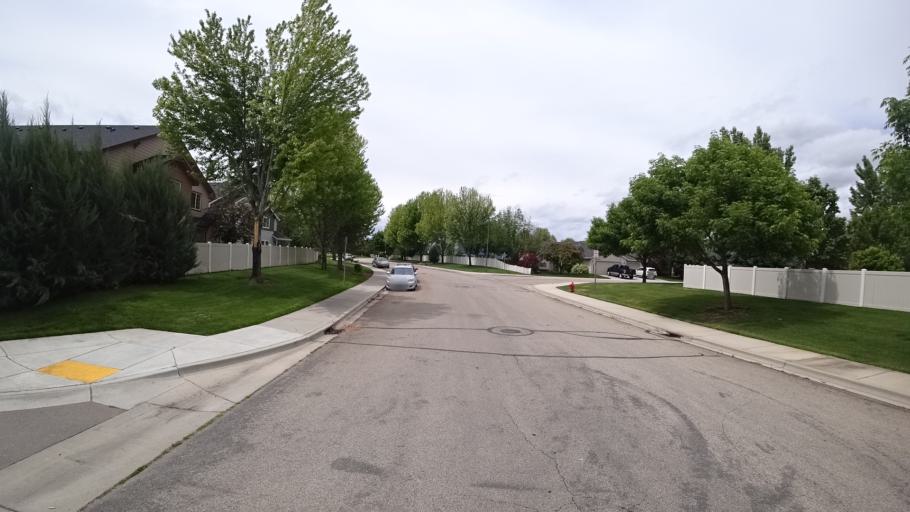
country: US
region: Idaho
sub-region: Ada County
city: Meridian
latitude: 43.6377
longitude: -116.3947
